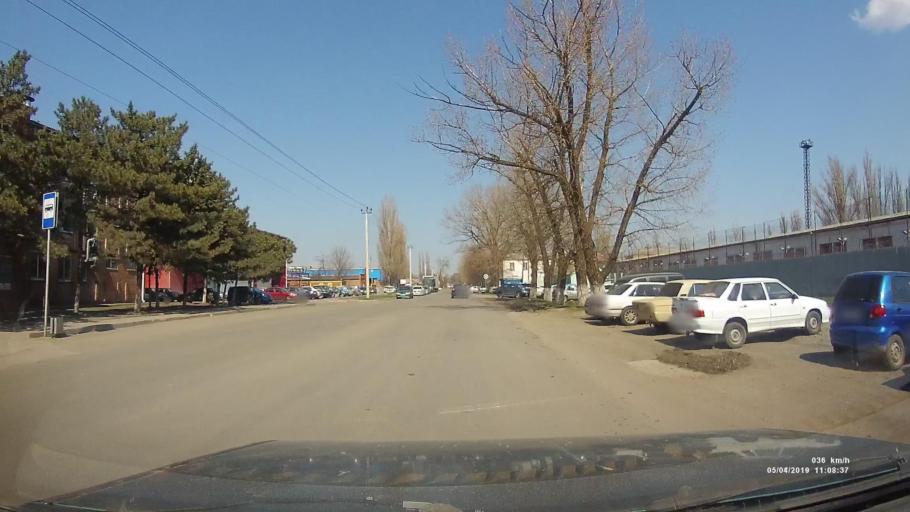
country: RU
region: Rostov
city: Azov
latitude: 47.0866
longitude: 39.4350
